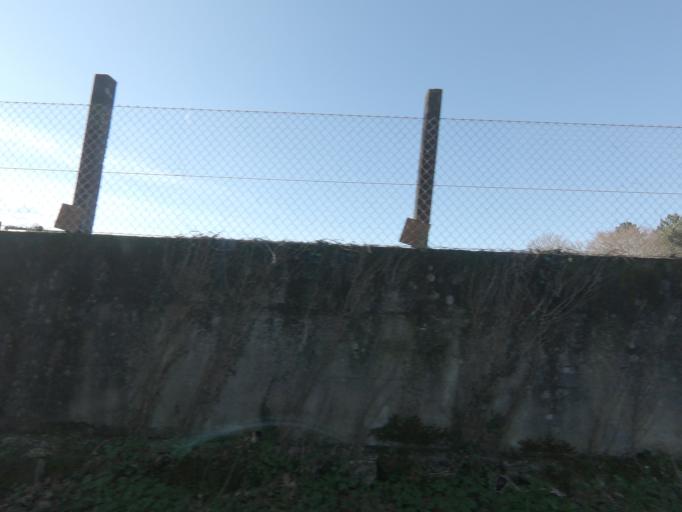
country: ES
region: Galicia
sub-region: Provincia da Coruna
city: Ribeira
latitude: 42.7118
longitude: -8.4443
